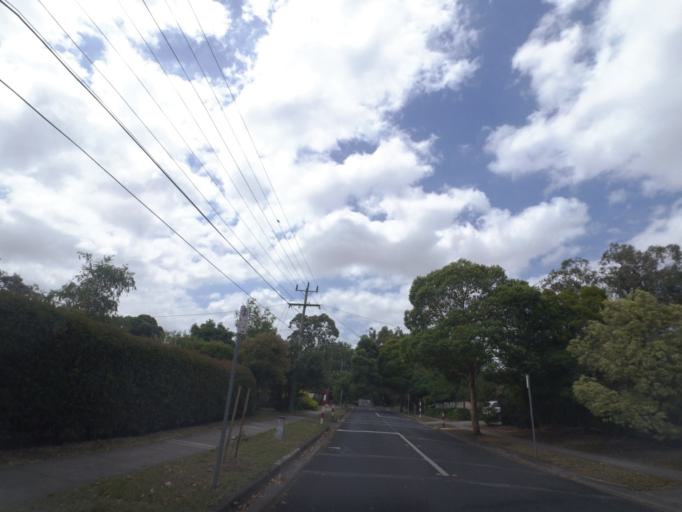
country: AU
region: Victoria
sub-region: Maroondah
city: Croydon South
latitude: -37.8089
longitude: 145.2826
